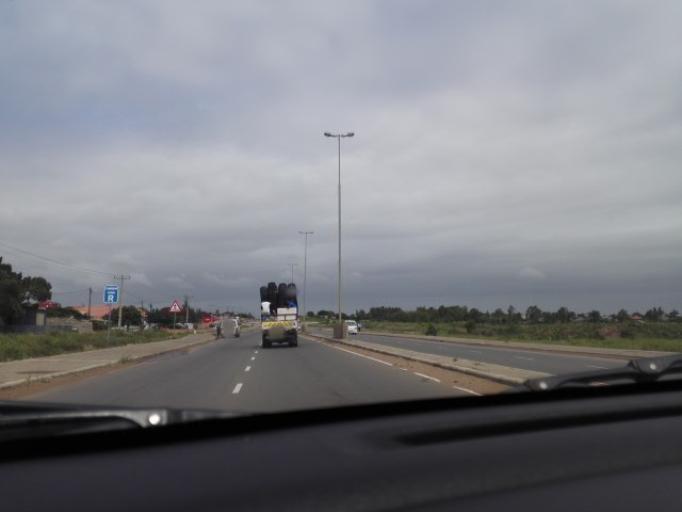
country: MZ
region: Maputo City
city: Maputo
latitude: -25.8274
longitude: 32.6049
